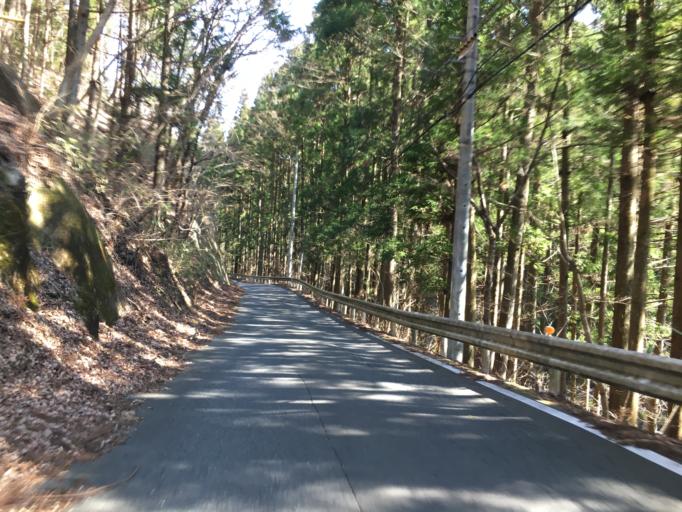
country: JP
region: Ibaraki
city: Takahagi
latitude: 36.8025
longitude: 140.6104
